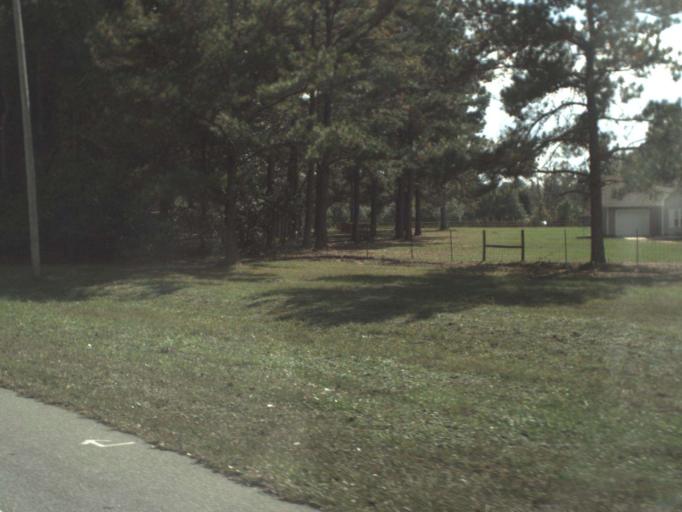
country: US
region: Florida
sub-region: Gadsden County
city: Gretna
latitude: 30.6739
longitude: -84.7035
